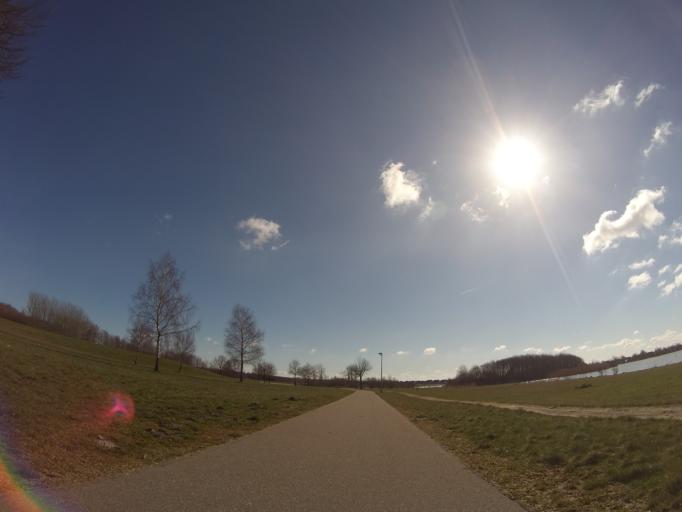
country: NL
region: Drenthe
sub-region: Gemeente Emmen
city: Emmen
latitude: 52.7398
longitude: 6.8966
